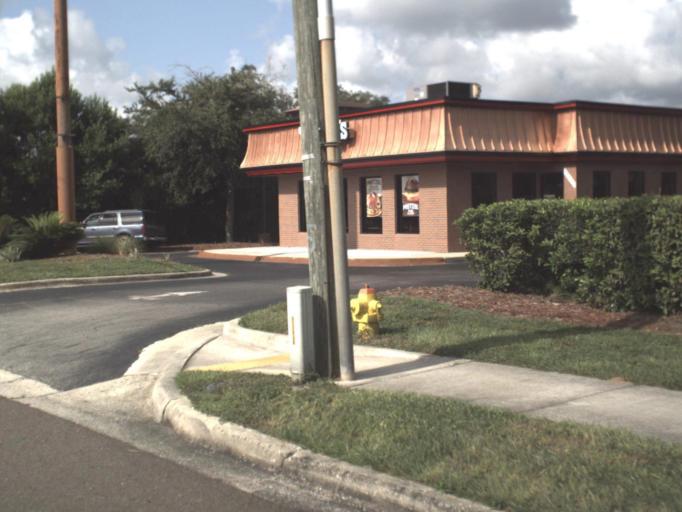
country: US
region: Florida
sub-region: Pasco County
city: Dade City
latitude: 28.3496
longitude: -82.1876
